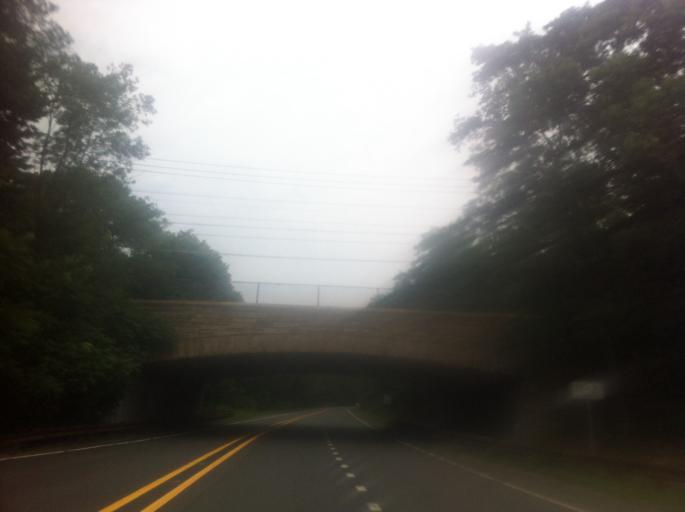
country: US
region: New York
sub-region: Nassau County
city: North Massapequa
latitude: 40.7213
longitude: -73.4633
